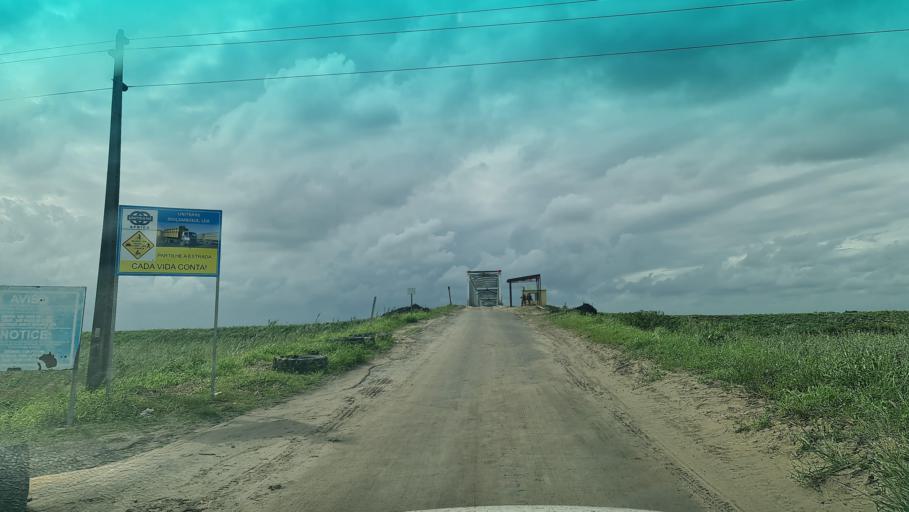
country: MZ
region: Maputo
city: Manhica
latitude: -25.4751
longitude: 32.8130
